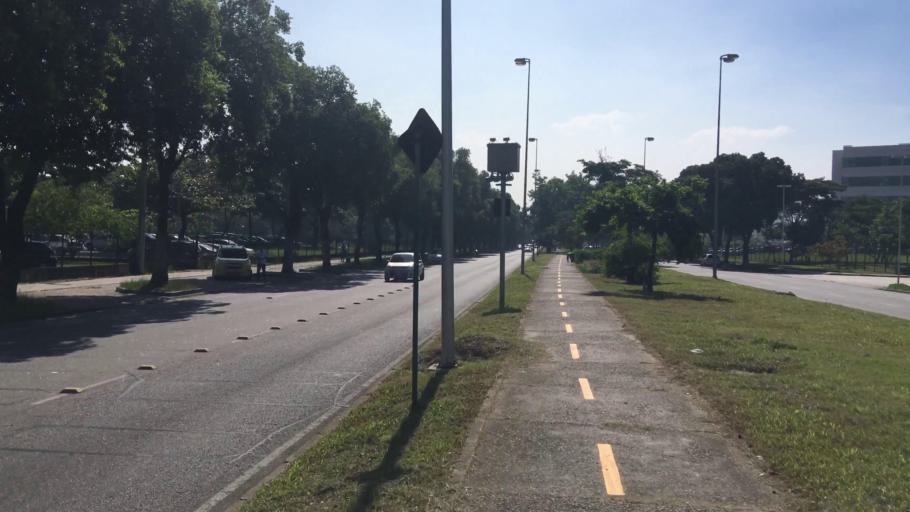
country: BR
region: Rio de Janeiro
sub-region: Rio De Janeiro
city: Rio de Janeiro
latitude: -22.8521
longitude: -43.2336
